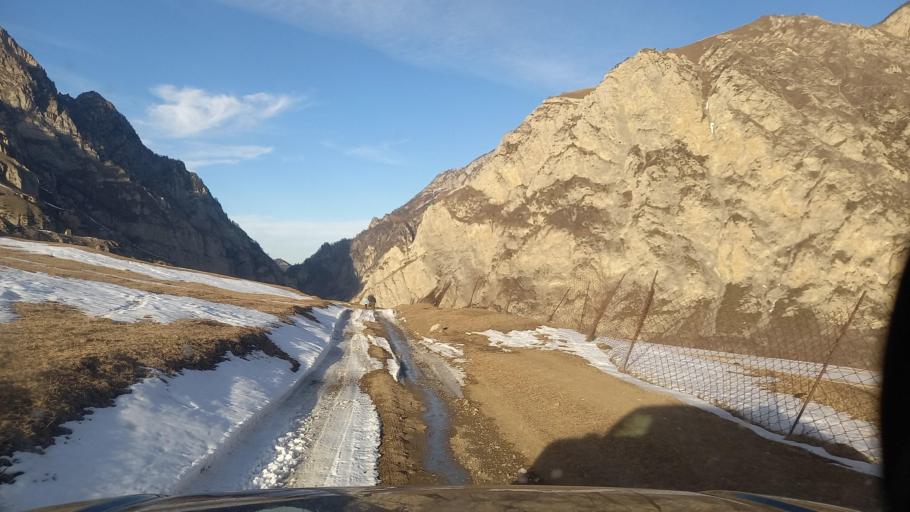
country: RU
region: Ingushetiya
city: Dzhayrakh
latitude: 42.8540
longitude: 44.5156
